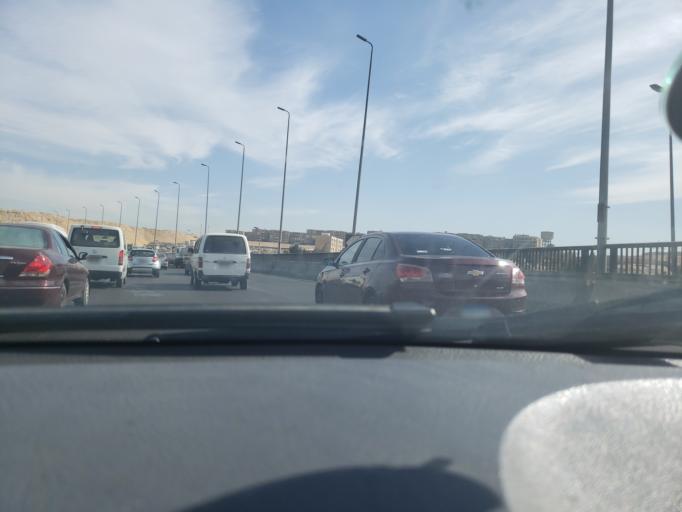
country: EG
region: Al Jizah
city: Al Jizah
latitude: 29.9957
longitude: 31.1082
